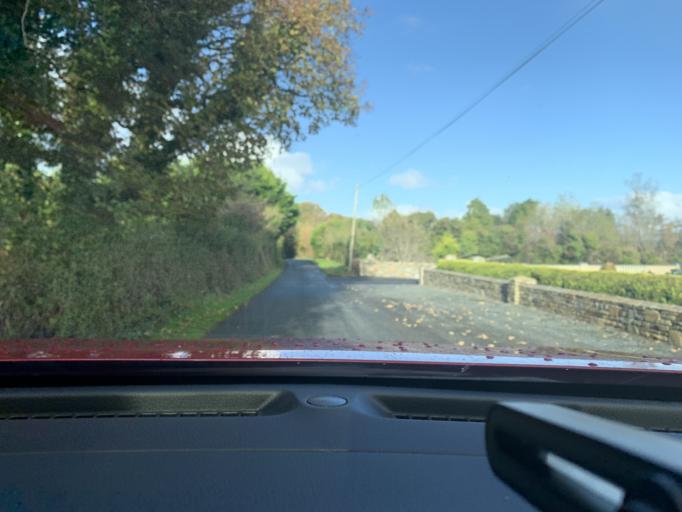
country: IE
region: Connaught
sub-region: Sligo
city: Ballymote
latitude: 54.0976
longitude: -8.4366
